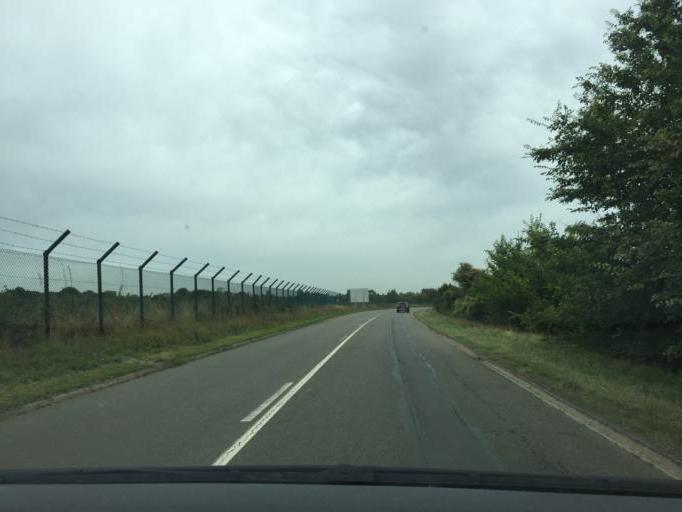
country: FR
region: Ile-de-France
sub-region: Departement des Yvelines
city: Les Loges-en-Josas
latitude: 48.7543
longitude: 2.1207
